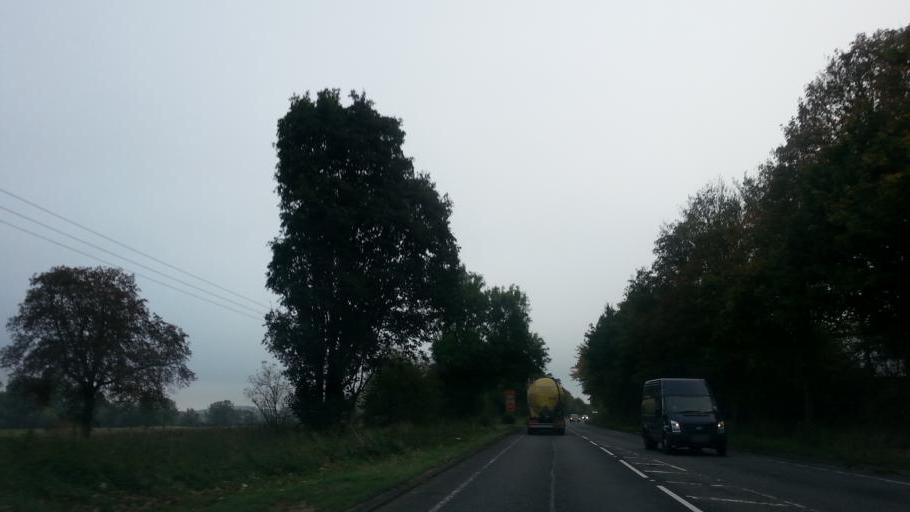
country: GB
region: England
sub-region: Northamptonshire
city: Oundle
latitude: 52.4812
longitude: -0.4583
